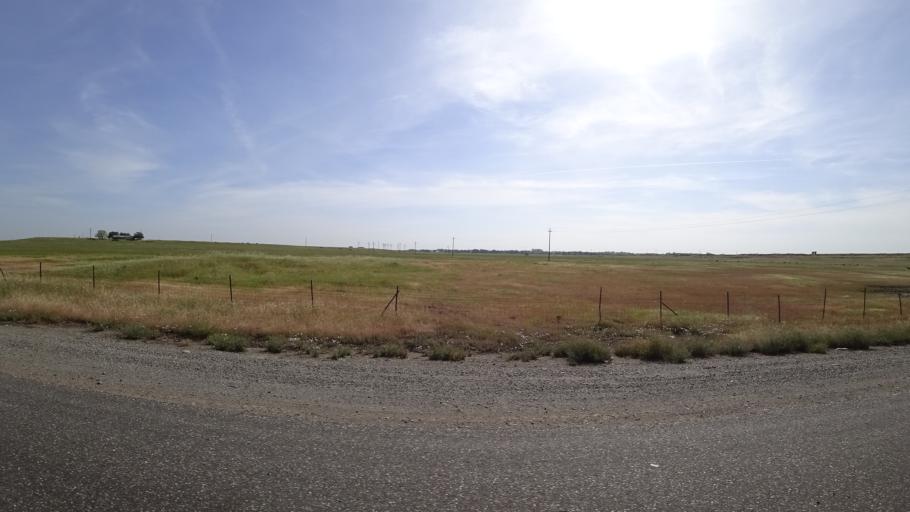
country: US
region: California
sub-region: Butte County
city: Durham
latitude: 39.6565
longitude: -121.7326
